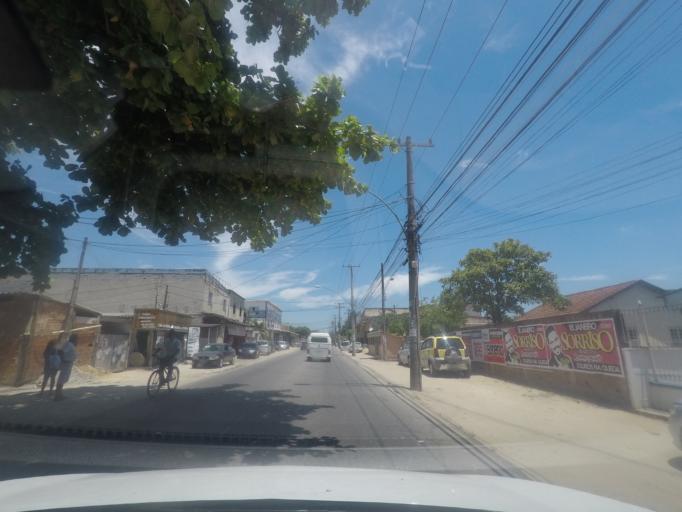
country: BR
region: Rio de Janeiro
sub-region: Itaguai
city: Itaguai
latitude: -22.9433
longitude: -43.6832
